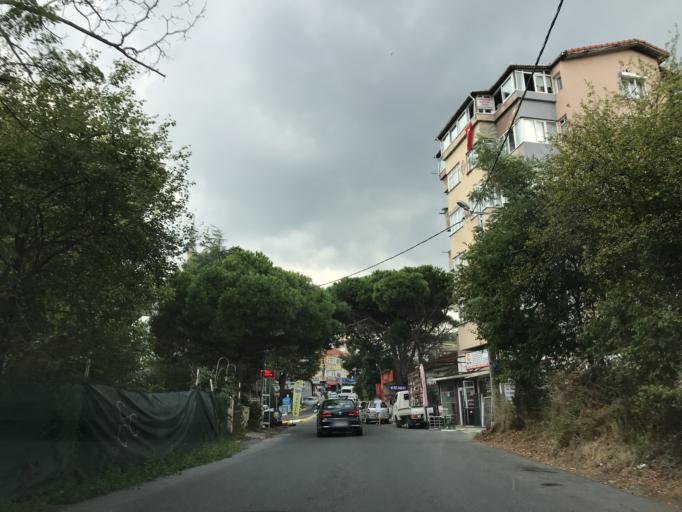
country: TR
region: Istanbul
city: Arikoey
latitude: 41.1781
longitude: 29.0513
